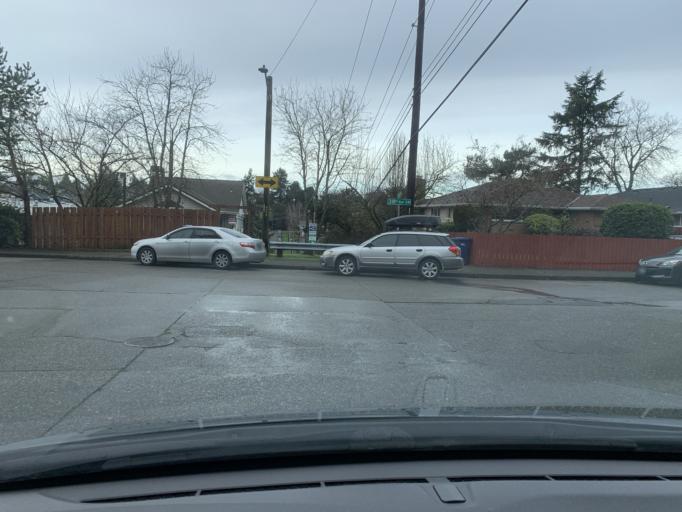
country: US
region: Washington
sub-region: King County
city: White Center
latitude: 47.5575
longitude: -122.3800
